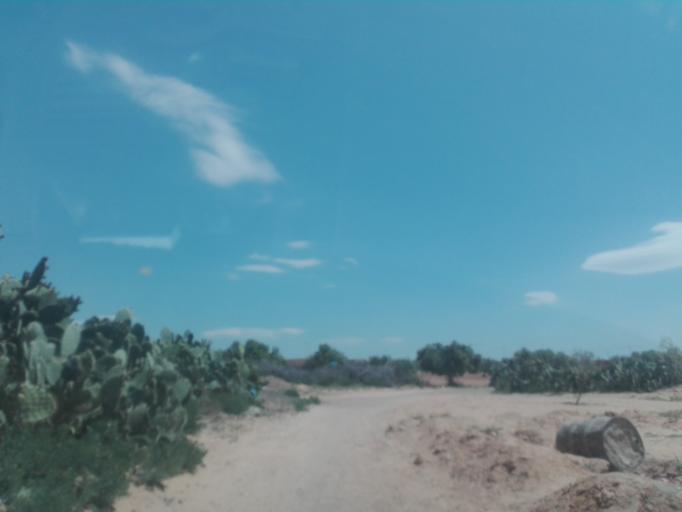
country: TN
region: Safaqis
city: Sfax
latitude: 34.6459
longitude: 10.5899
